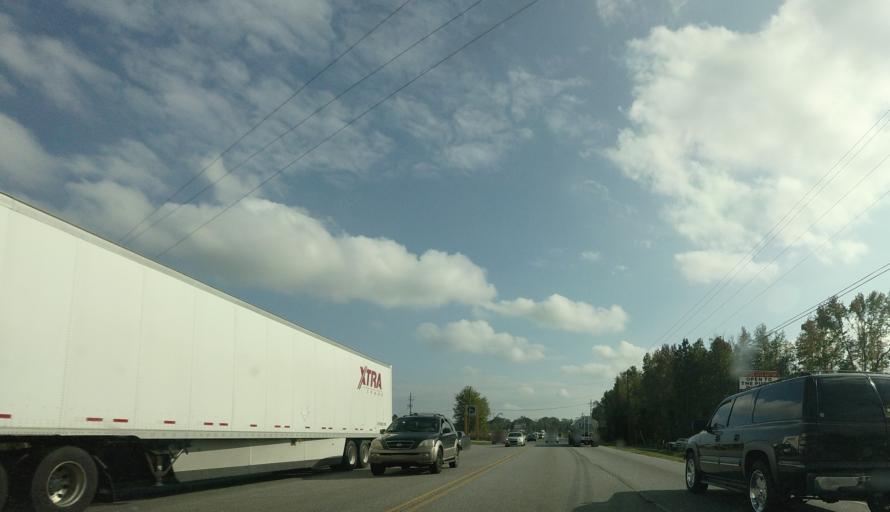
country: US
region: Georgia
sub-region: Bibb County
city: Macon
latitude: 32.7771
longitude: -83.6622
